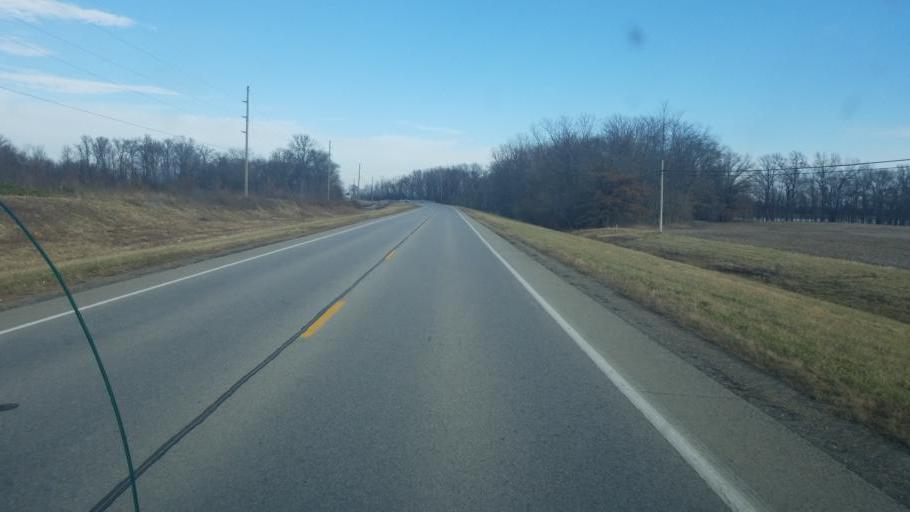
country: US
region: Illinois
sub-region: White County
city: Carmi
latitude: 38.1071
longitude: -88.1277
